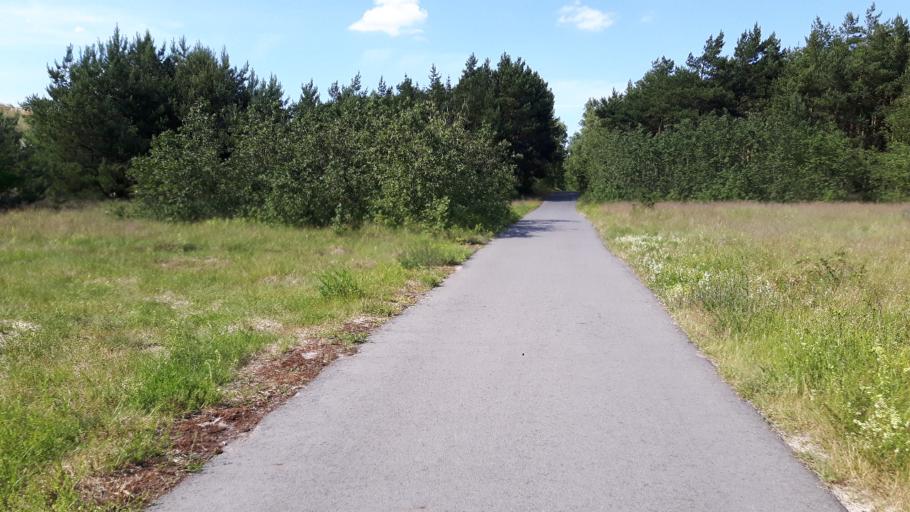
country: LT
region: Klaipedos apskritis
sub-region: Klaipeda
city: Klaipeda
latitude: 55.6855
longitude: 21.1039
